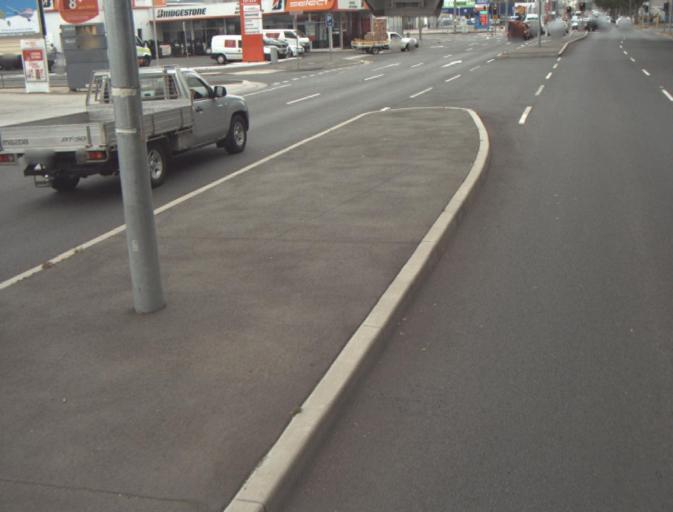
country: AU
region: Tasmania
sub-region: Launceston
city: Launceston
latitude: -41.4254
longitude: 147.1370
